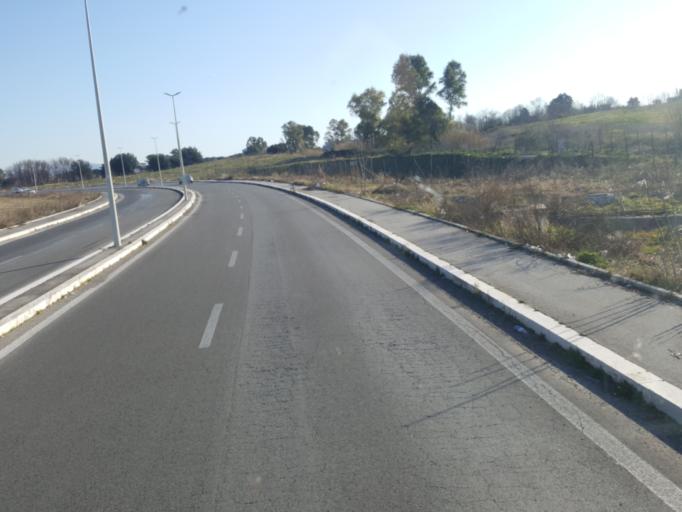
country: IT
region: Latium
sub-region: Citta metropolitana di Roma Capitale
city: Setteville
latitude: 41.8864
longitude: 12.6036
